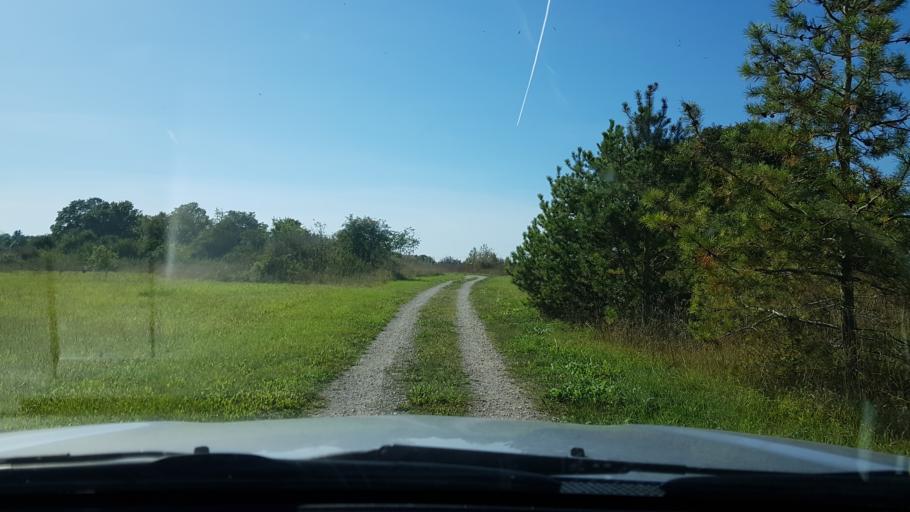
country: EE
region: Ida-Virumaa
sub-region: Sillamaee linn
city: Sillamae
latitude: 59.3906
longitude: 27.8092
